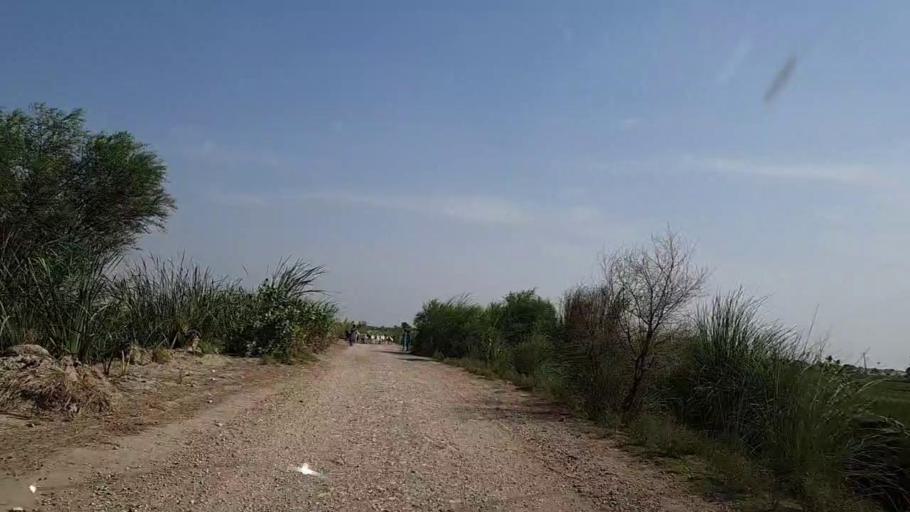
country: PK
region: Sindh
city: Khanpur
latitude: 27.7189
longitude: 69.3609
